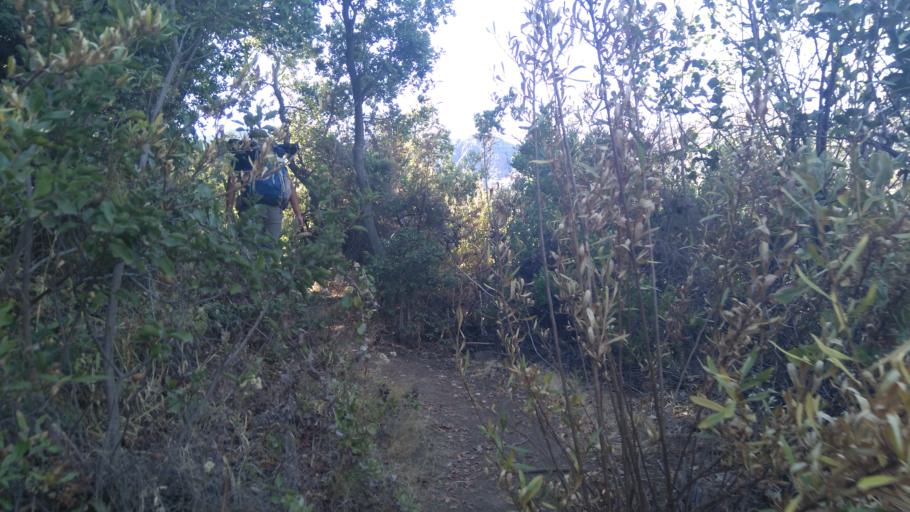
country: CL
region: Santiago Metropolitan
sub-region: Provincia de Cordillera
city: Puente Alto
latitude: -33.7135
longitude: -70.4583
